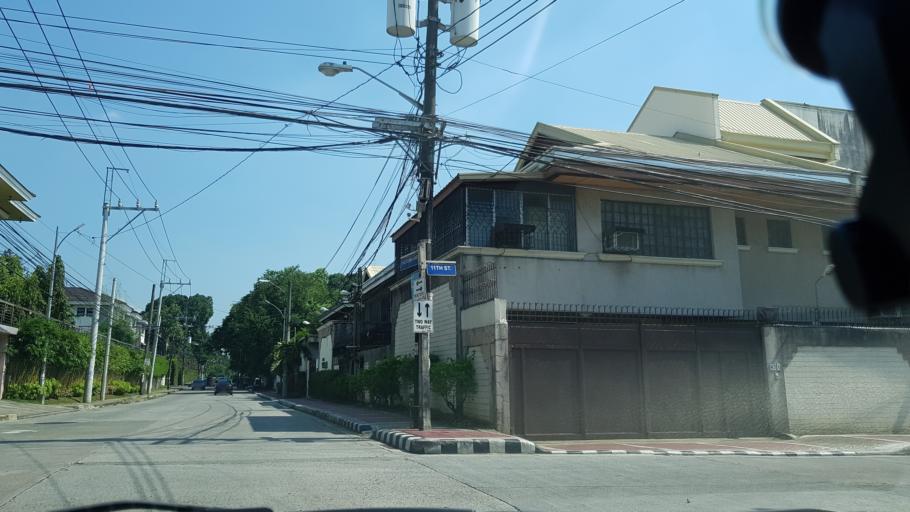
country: PH
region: Metro Manila
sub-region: San Juan
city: San Juan
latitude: 14.6186
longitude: 121.0259
